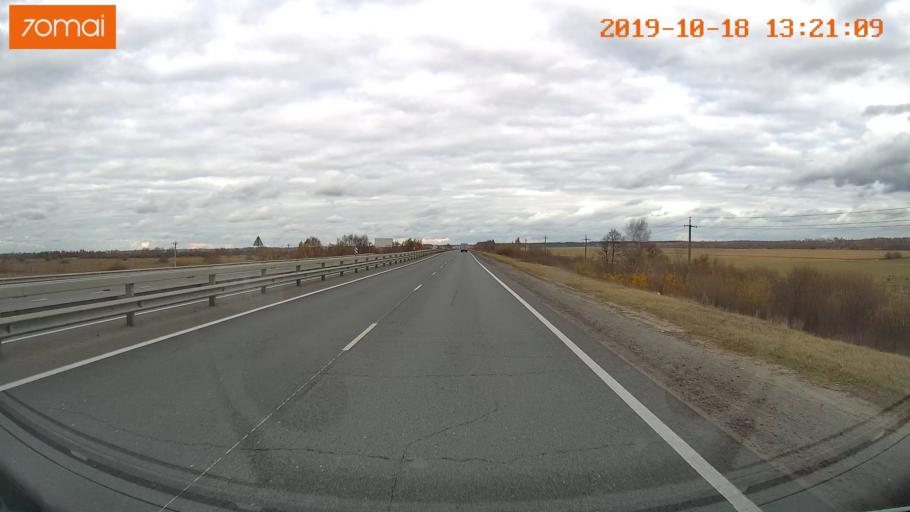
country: RU
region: Rjazan
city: Polyany
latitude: 54.6927
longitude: 39.8384
